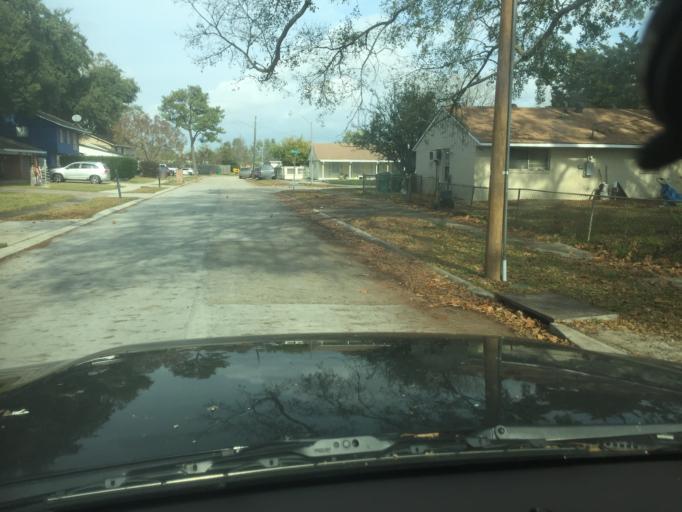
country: US
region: Louisiana
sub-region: Jefferson Parish
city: Avondale
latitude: 29.9143
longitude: -90.2055
